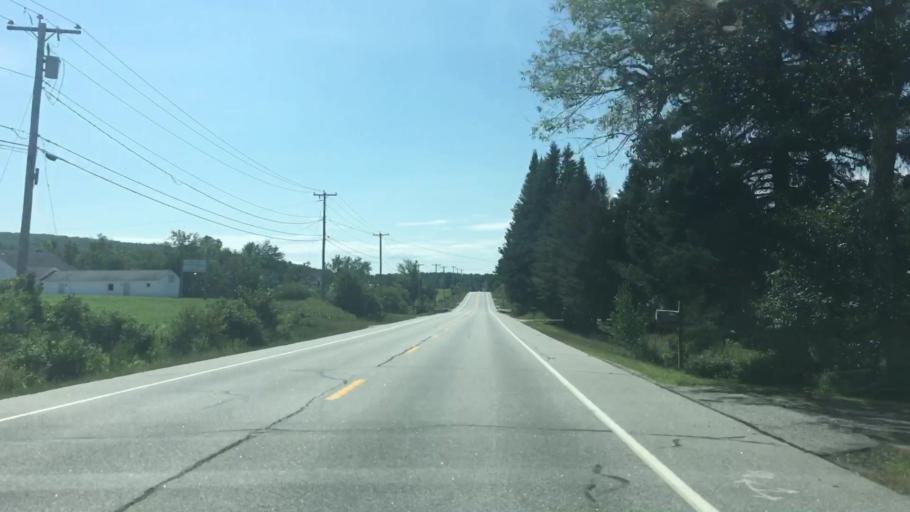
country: US
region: Maine
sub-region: Kennebec County
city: Monmouth
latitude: 44.1765
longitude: -70.0006
